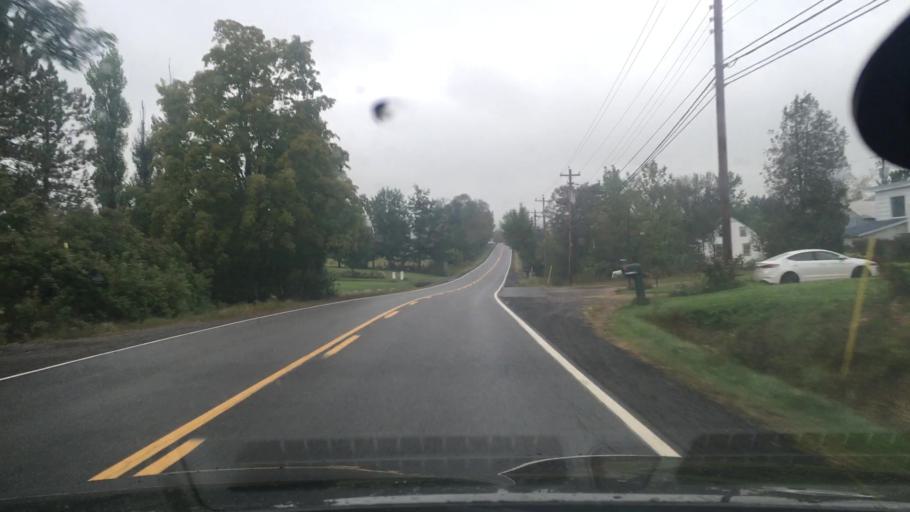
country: CA
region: Nova Scotia
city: Windsor
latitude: 44.9474
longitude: -64.1774
